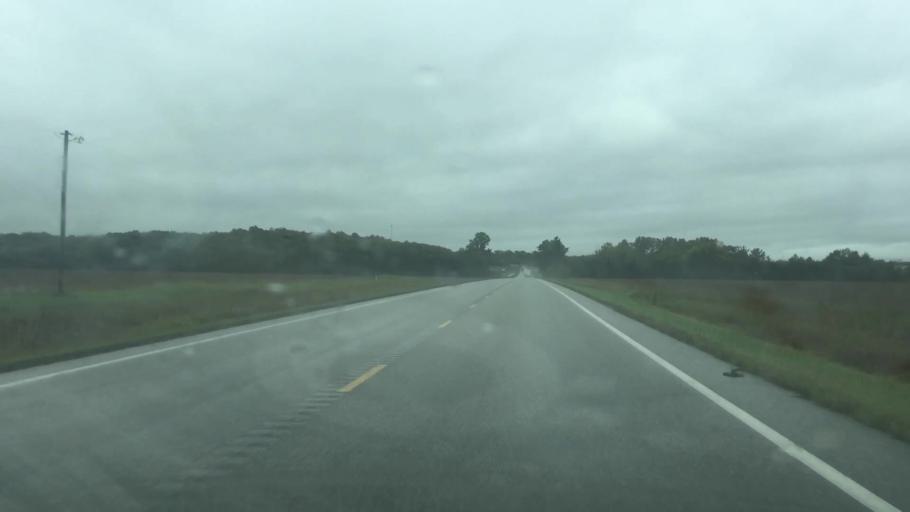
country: US
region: Kansas
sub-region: Anderson County
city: Garnett
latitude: 38.3746
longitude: -95.1149
